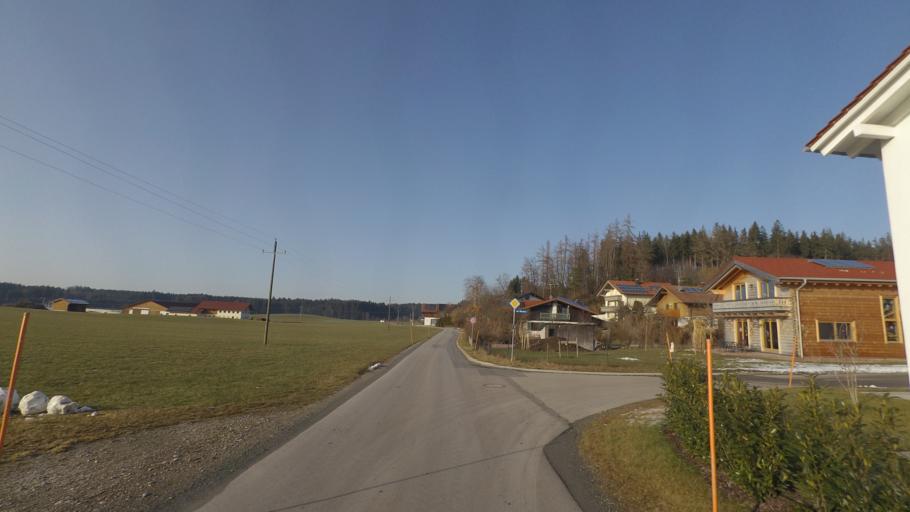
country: DE
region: Bavaria
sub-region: Upper Bavaria
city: Nussdorf
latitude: 47.9098
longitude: 12.5914
